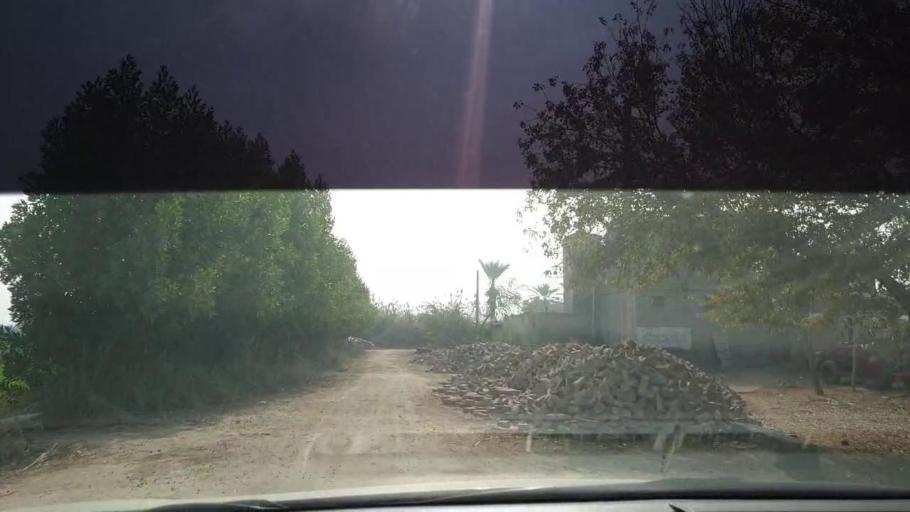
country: PK
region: Sindh
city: Berani
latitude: 25.8416
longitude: 68.8500
